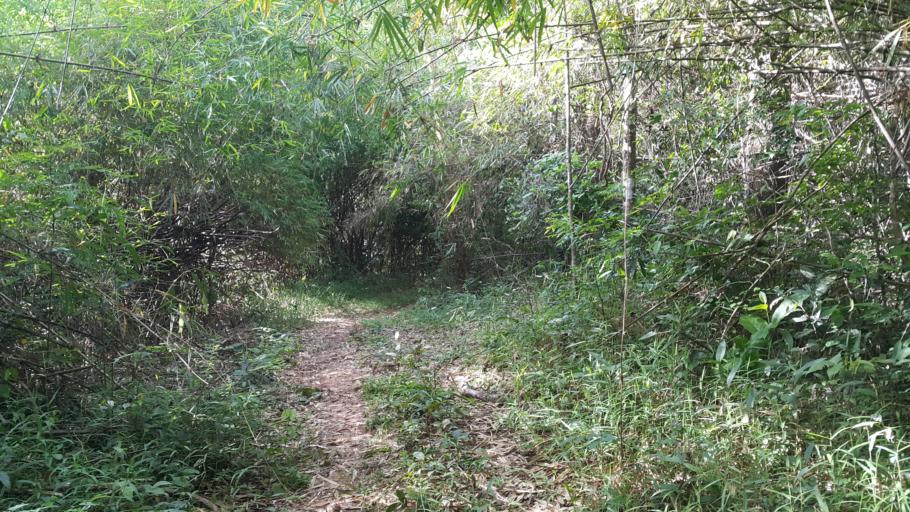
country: TH
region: Loei
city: Na Haeo
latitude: 17.5533
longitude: 101.0015
